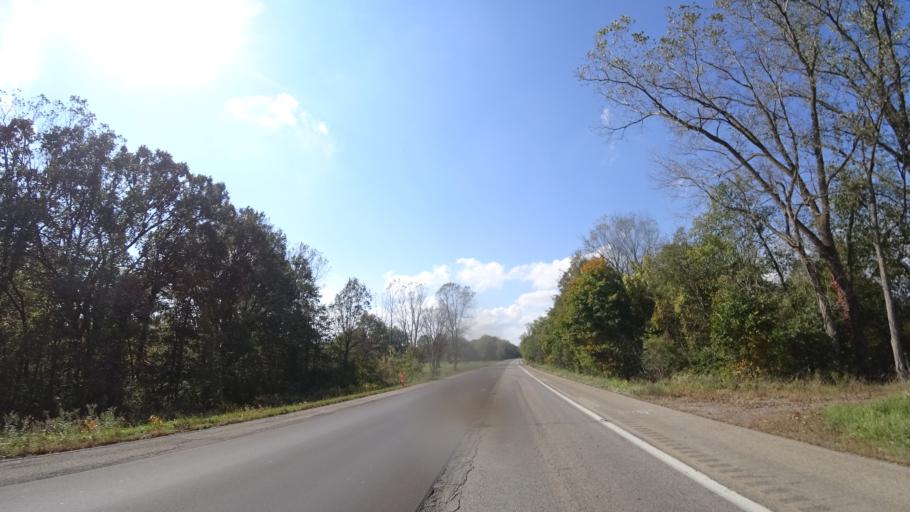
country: US
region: Michigan
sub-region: Calhoun County
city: Homer
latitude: 42.1306
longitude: -84.8949
